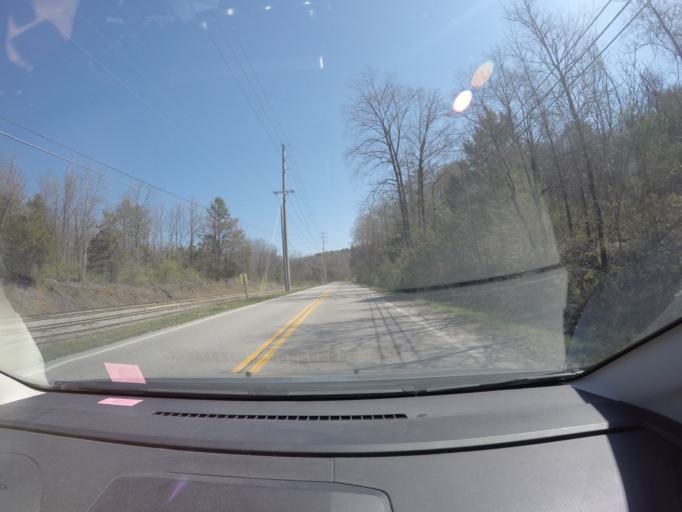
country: US
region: Tennessee
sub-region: Hamilton County
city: Signal Mountain
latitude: 35.1029
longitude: -85.3363
